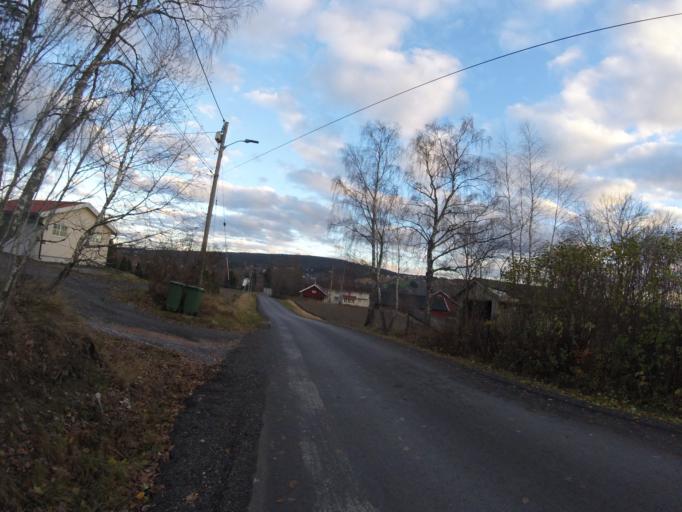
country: NO
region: Akershus
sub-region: Skedsmo
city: Leirsund
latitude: 59.9965
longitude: 11.0818
